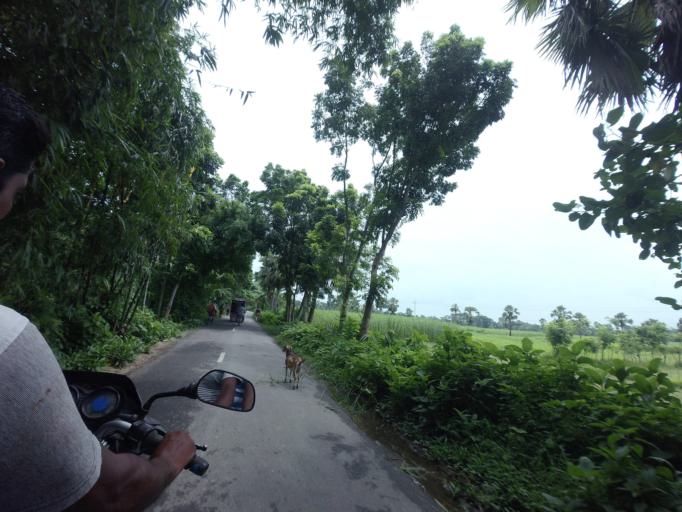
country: BD
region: Khulna
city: Kalia
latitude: 23.0940
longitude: 89.6544
